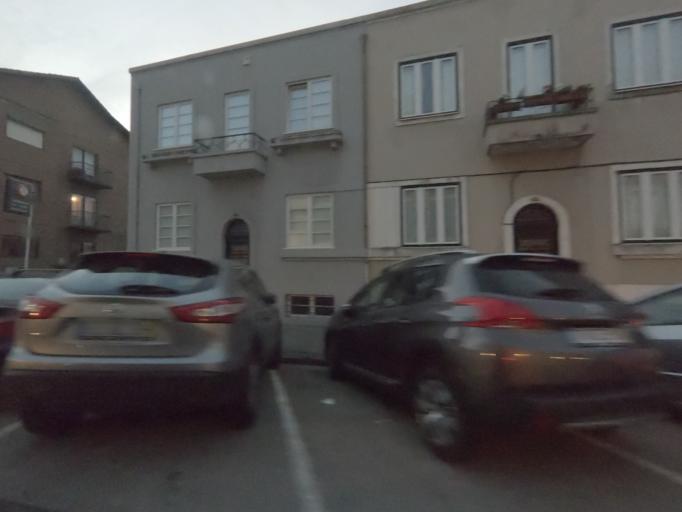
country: PT
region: Porto
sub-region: Matosinhos
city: Matosinhos
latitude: 41.1534
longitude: -8.6742
